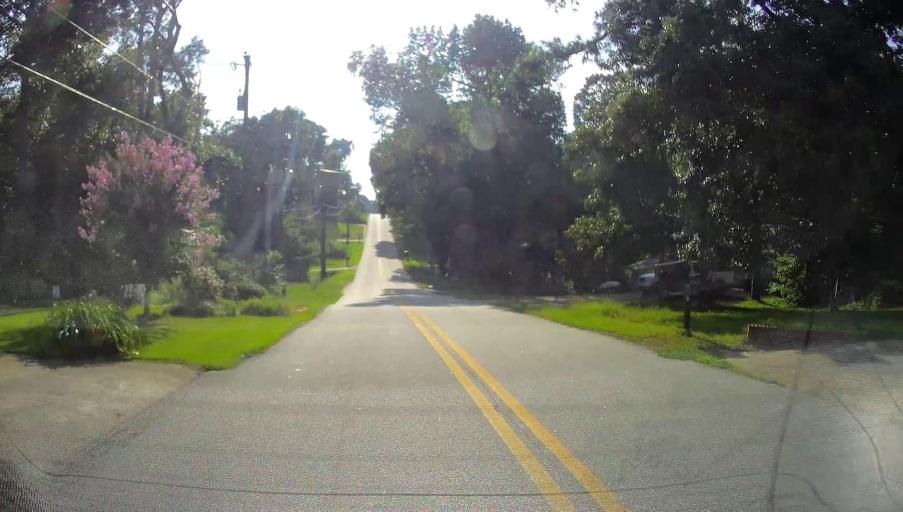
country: US
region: Georgia
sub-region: Houston County
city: Warner Robins
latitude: 32.5994
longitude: -83.6435
